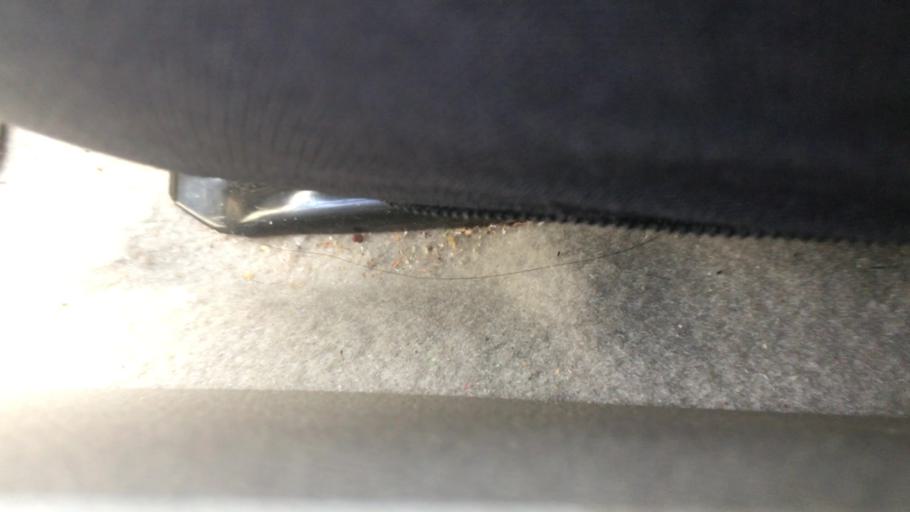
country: US
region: Maryland
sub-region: Montgomery County
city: Germantown
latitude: 39.1764
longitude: -77.2639
